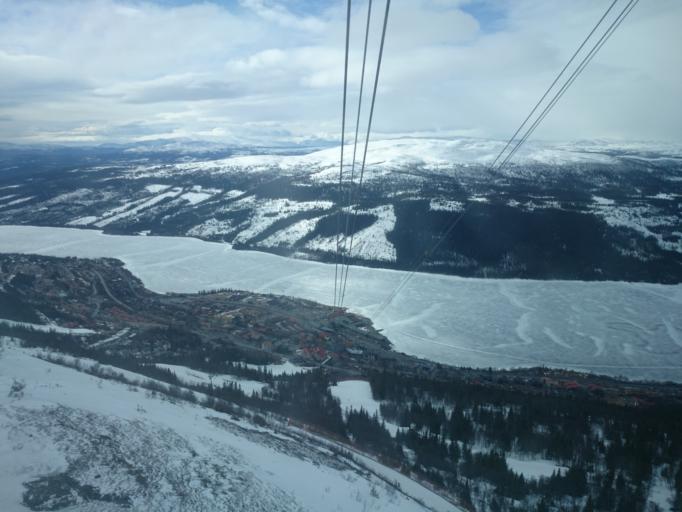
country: SE
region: Jaemtland
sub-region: Are Kommun
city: Are
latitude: 63.4126
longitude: 13.0778
